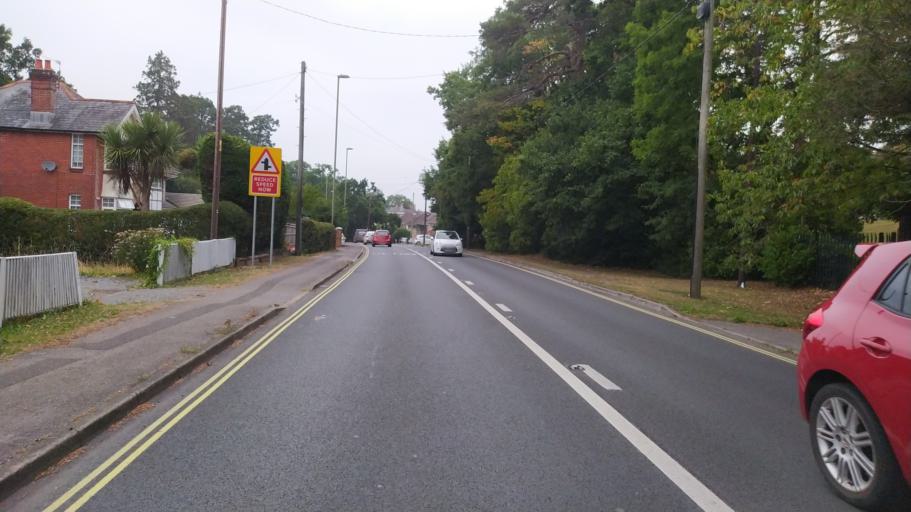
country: GB
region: England
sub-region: Hampshire
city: West End
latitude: 50.9193
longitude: -1.3322
